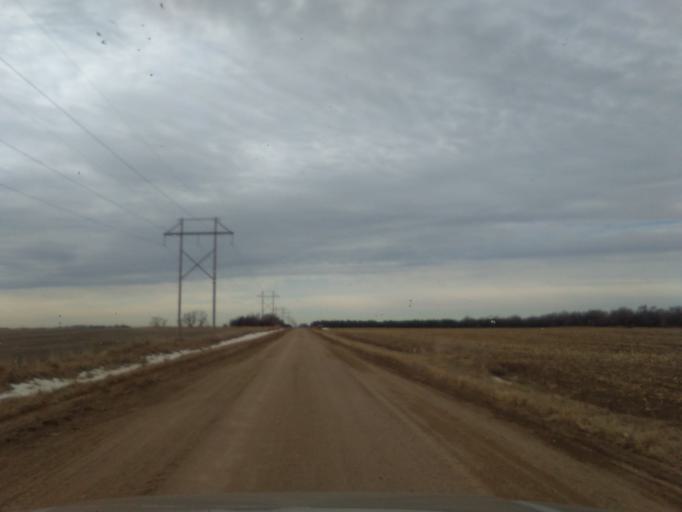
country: US
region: Nebraska
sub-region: Buffalo County
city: Gibbon
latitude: 40.6549
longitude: -98.7669
